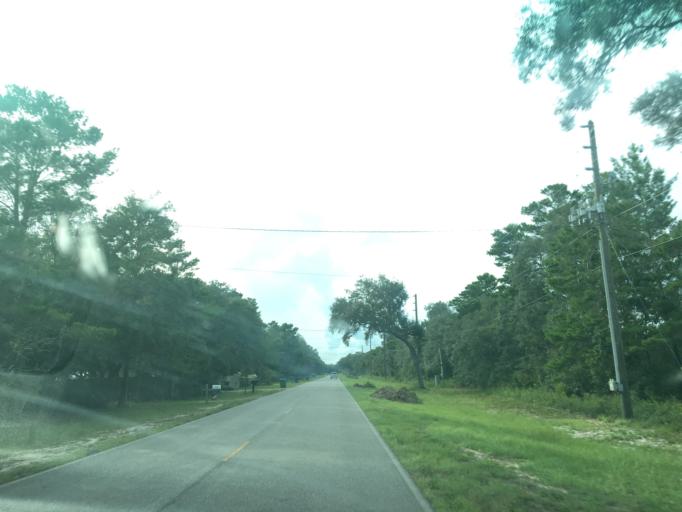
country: US
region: Florida
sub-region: Wakulla County
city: Crawfordville
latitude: 29.9074
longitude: -84.3575
